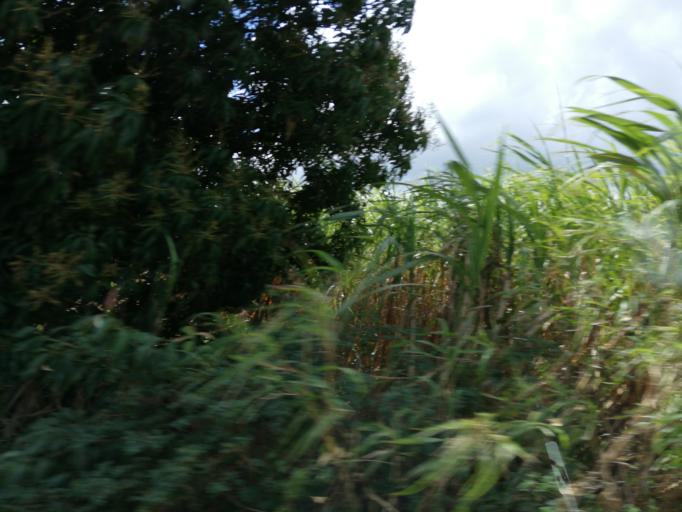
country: MU
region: Riviere du Rempart
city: Esperance Trebuchet
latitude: -20.0715
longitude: 57.6415
